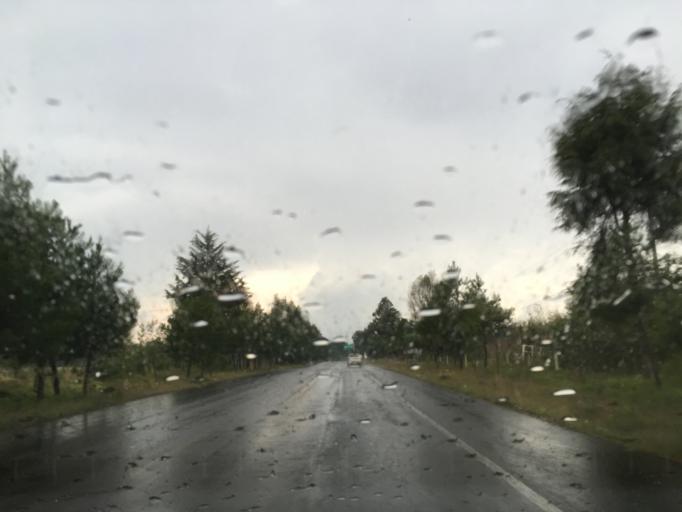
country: MX
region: Michoacan
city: Angahuan
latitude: 19.5249
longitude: -102.1862
